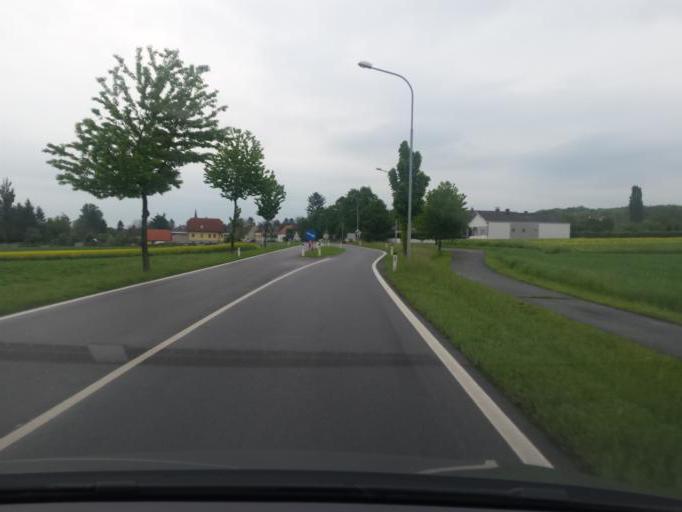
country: AT
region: Burgenland
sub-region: Politischer Bezirk Oberpullendorf
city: Oberpullendorf
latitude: 47.4787
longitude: 16.5332
